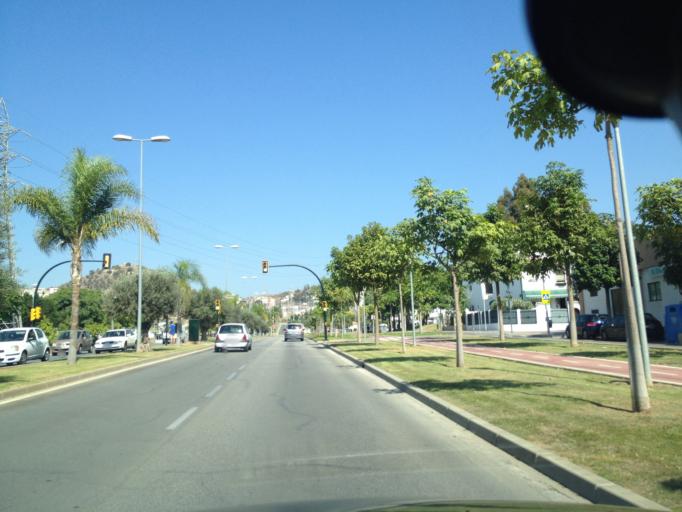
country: ES
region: Andalusia
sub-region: Provincia de Malaga
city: Malaga
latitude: 36.7226
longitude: -4.4698
